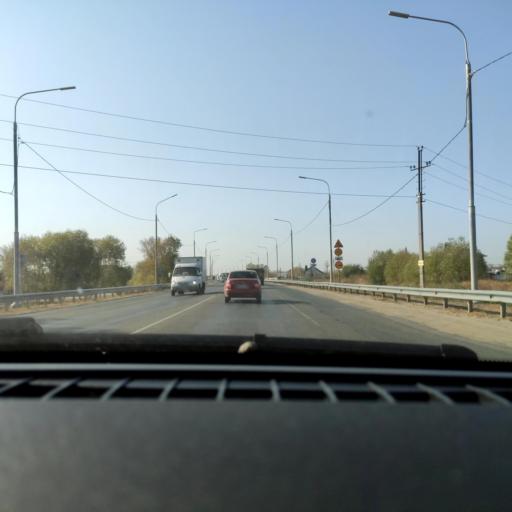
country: RU
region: Voronezj
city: Somovo
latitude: 51.6897
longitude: 39.3617
